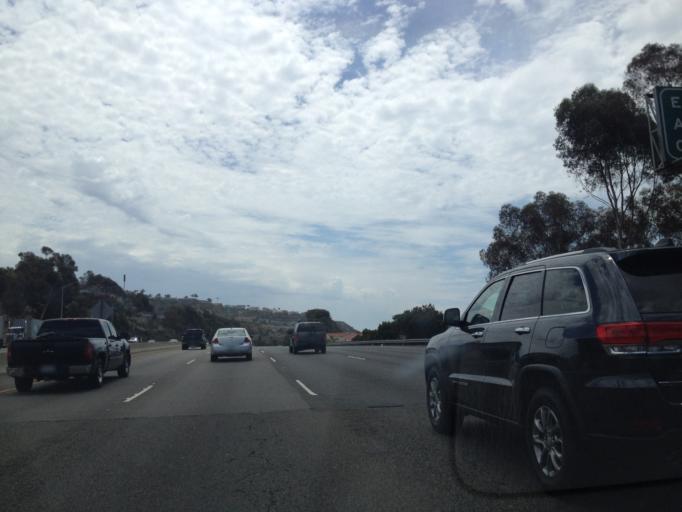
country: US
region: California
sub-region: Orange County
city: San Clemente
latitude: 33.4309
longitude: -117.6144
